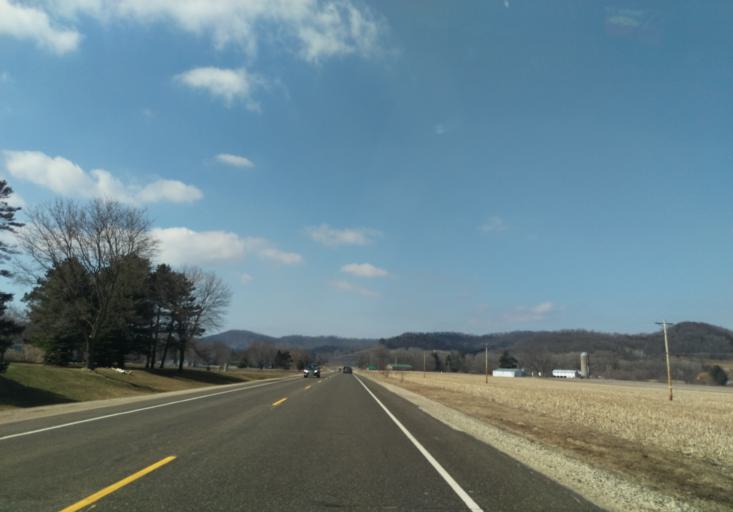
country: US
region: Wisconsin
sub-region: La Crosse County
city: La Crosse
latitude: 43.7617
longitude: -91.1363
